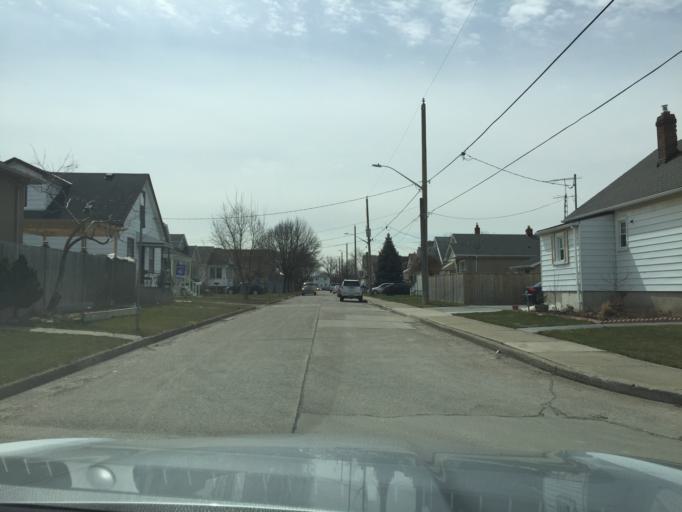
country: CA
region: Ontario
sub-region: Regional Municipality of Niagara
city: St. Catharines
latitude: 43.1792
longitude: -79.2226
